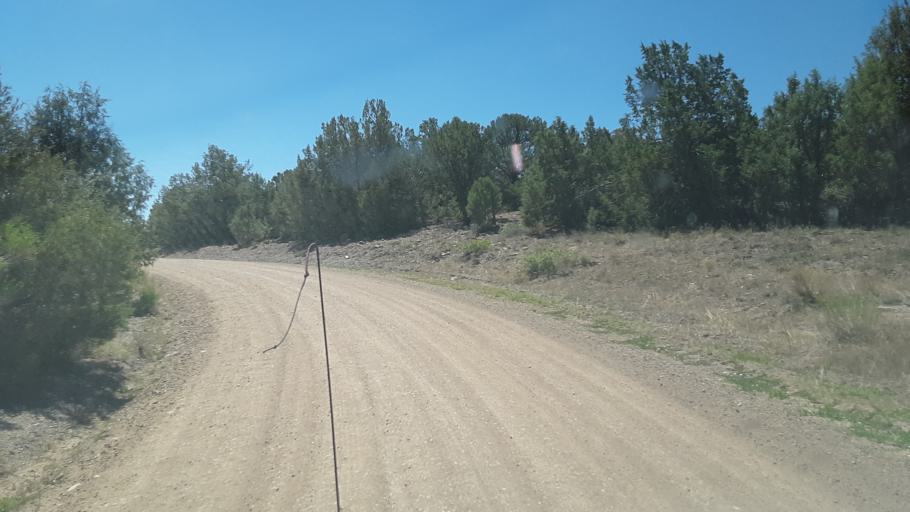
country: US
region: Colorado
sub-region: Custer County
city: Westcliffe
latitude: 38.2986
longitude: -105.6154
